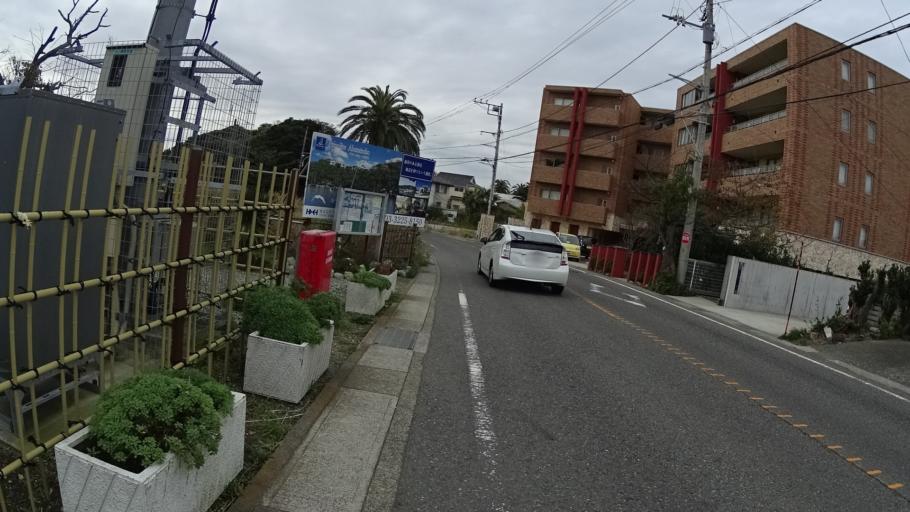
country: JP
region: Kanagawa
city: Miura
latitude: 35.1609
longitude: 139.6166
